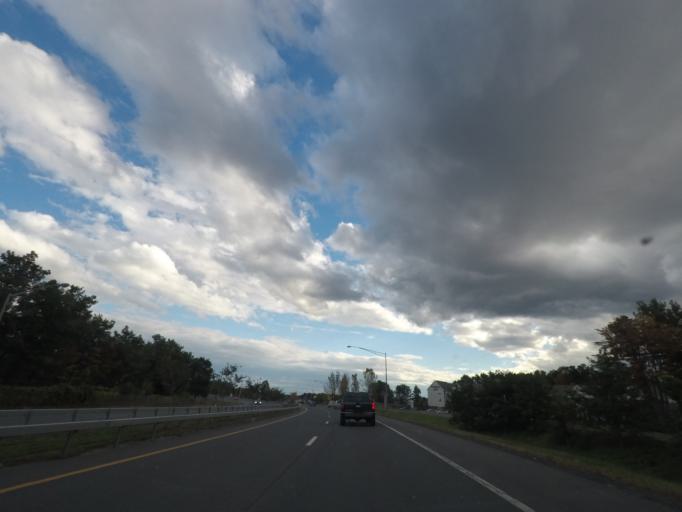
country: US
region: New York
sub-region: Albany County
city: McKownville
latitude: 42.6939
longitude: -73.8493
